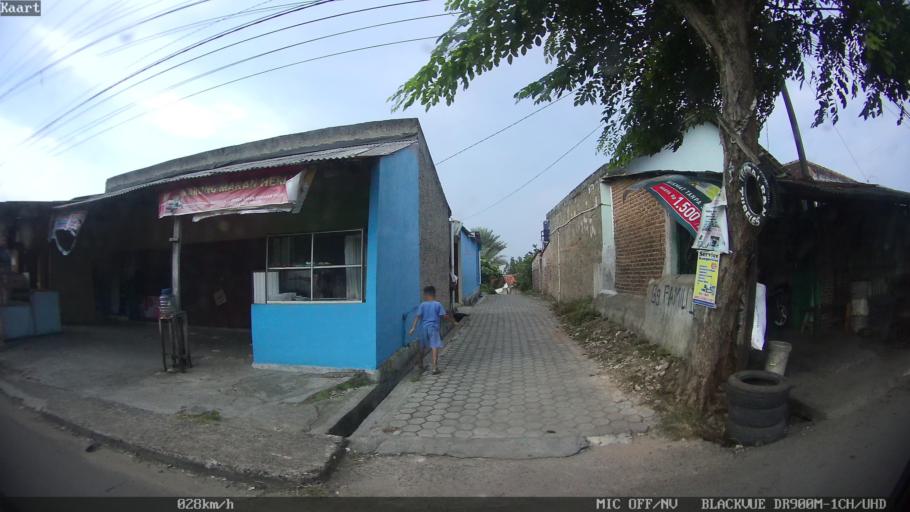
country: ID
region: Lampung
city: Kedaton
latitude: -5.3895
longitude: 105.2077
